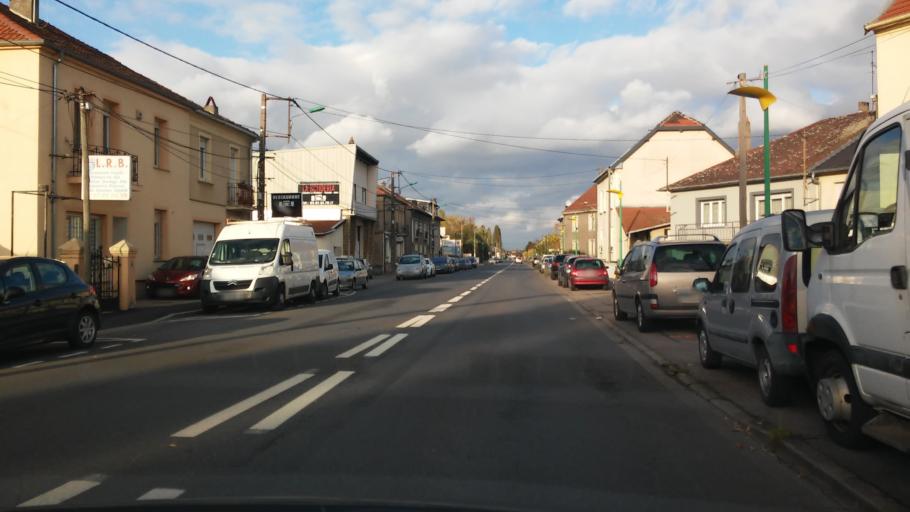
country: FR
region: Lorraine
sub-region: Departement de la Moselle
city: Maizieres-les-Metz
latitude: 49.2173
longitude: 6.1609
